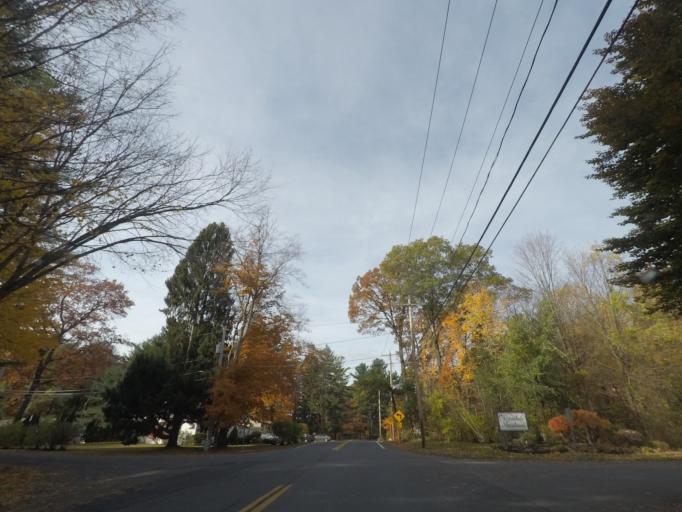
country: US
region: New York
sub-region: Schenectady County
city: Rotterdam
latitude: 42.7554
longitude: -73.9448
